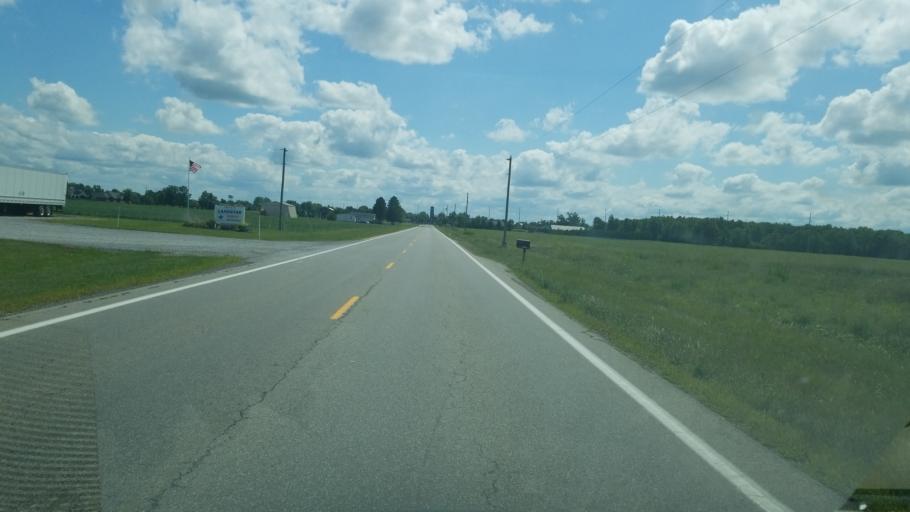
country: US
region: Ohio
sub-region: Putnam County
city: Kalida
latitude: 40.9995
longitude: -84.1978
